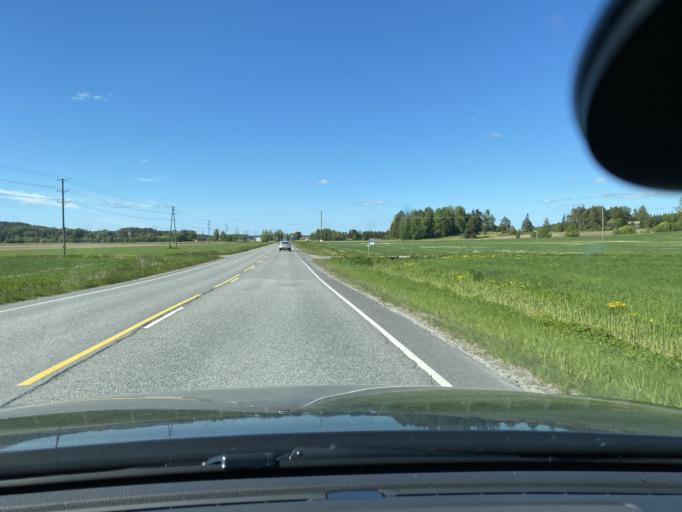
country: FI
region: Varsinais-Suomi
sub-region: Turku
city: Paimio
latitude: 60.4130
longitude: 22.6649
